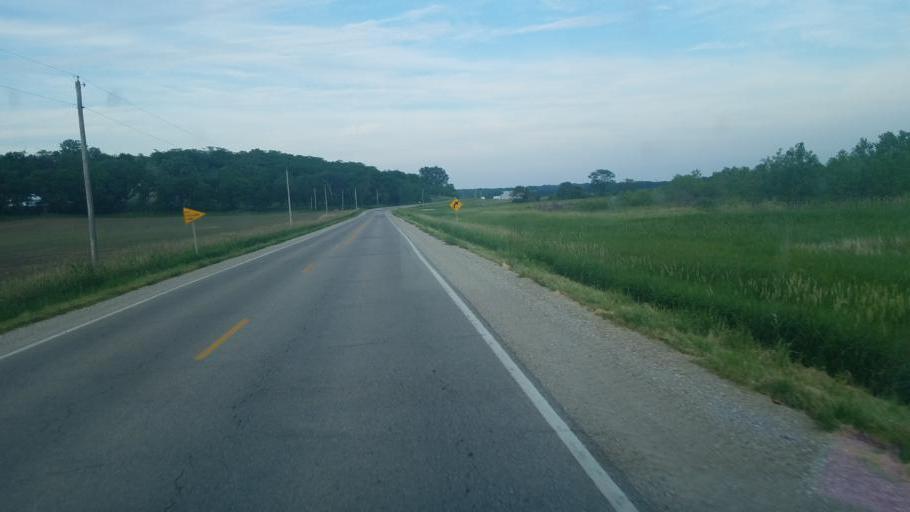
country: US
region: Iowa
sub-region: Benton County
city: Belle Plaine
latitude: 41.9203
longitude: -92.3795
